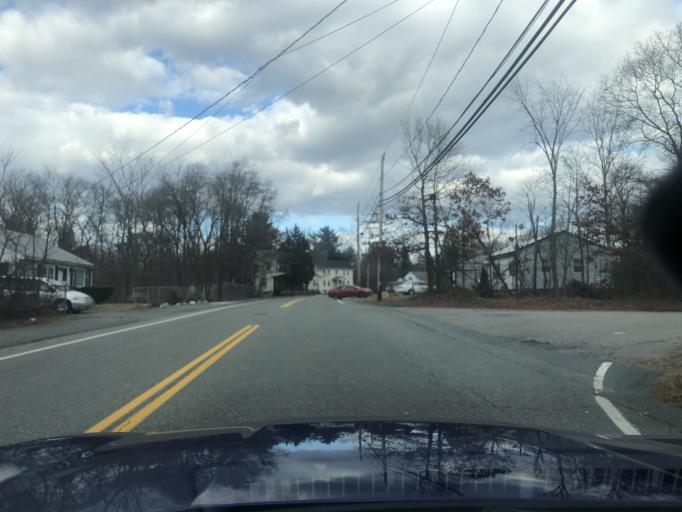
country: US
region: Massachusetts
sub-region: Plymouth County
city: Brockton
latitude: 42.1029
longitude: -71.0067
